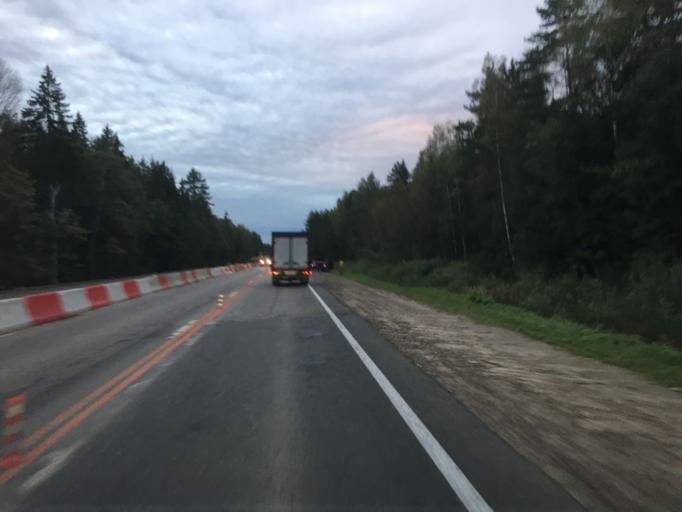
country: RU
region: Kaluga
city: Detchino
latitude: 54.7105
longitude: 36.2902
